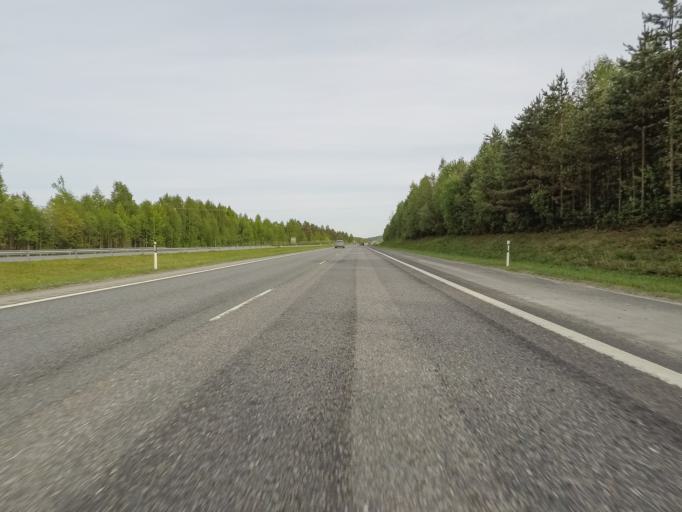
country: FI
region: Haeme
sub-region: Haemeenlinna
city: Parola
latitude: 61.0390
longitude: 24.3747
